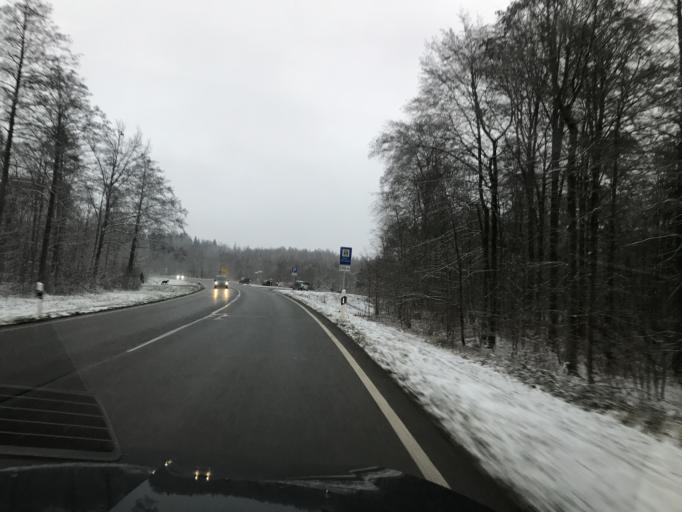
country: DE
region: Baden-Wuerttemberg
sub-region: Regierungsbezirk Stuttgart
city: Altbach
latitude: 48.7355
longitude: 9.4024
